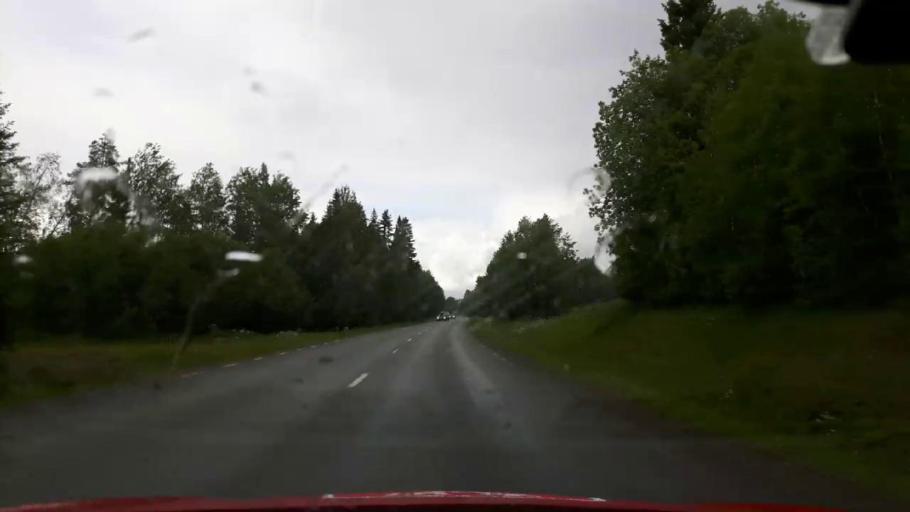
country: SE
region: Jaemtland
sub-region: Krokoms Kommun
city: Krokom
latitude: 63.4464
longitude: 14.1958
